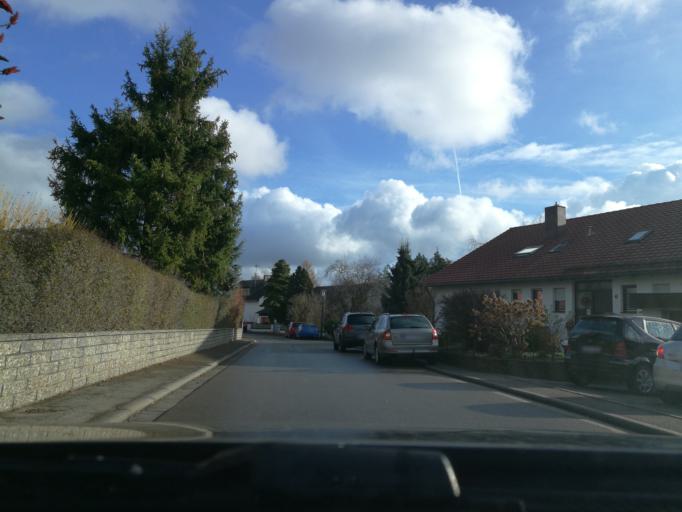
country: DE
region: Bavaria
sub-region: Regierungsbezirk Mittelfranken
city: Spalt
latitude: 49.2200
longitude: 10.8893
